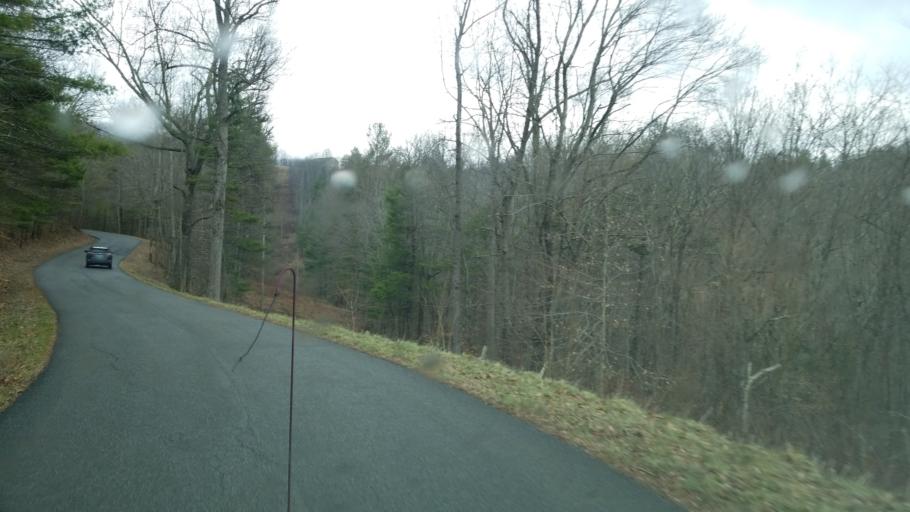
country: US
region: Virginia
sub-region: Giles County
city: Pearisburg
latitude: 37.2236
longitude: -80.7000
